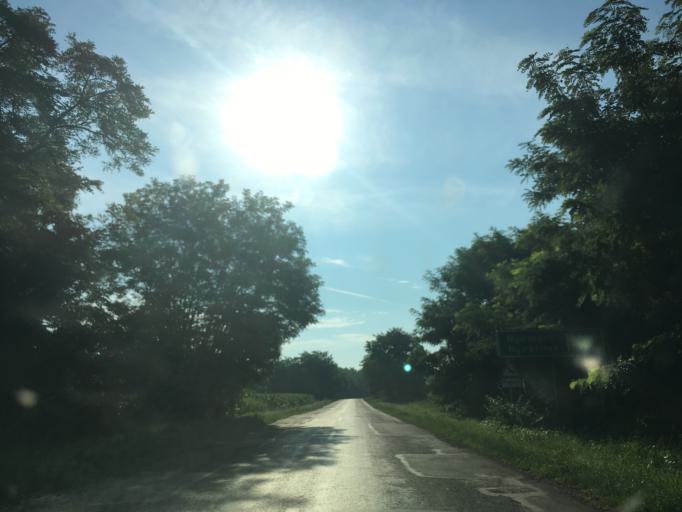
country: HU
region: Hajdu-Bihar
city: Nyiradony
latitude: 47.6910
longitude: 21.9235
